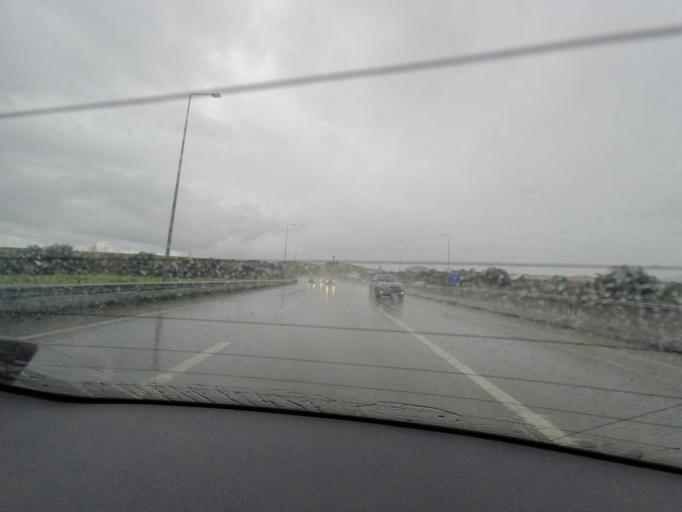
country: PT
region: Lisbon
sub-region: Sintra
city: Sintra
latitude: 38.8134
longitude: -9.3581
